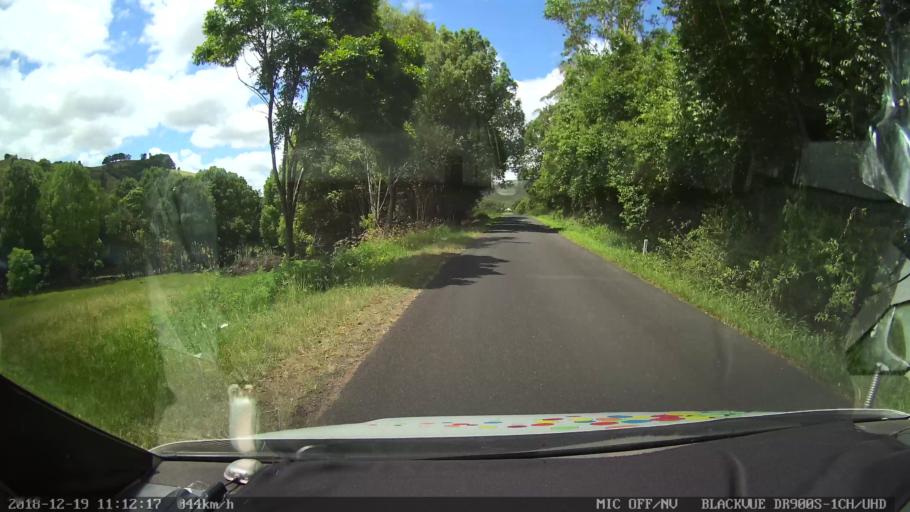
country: AU
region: New South Wales
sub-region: Lismore Municipality
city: Nimbin
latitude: -28.6478
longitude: 153.2606
